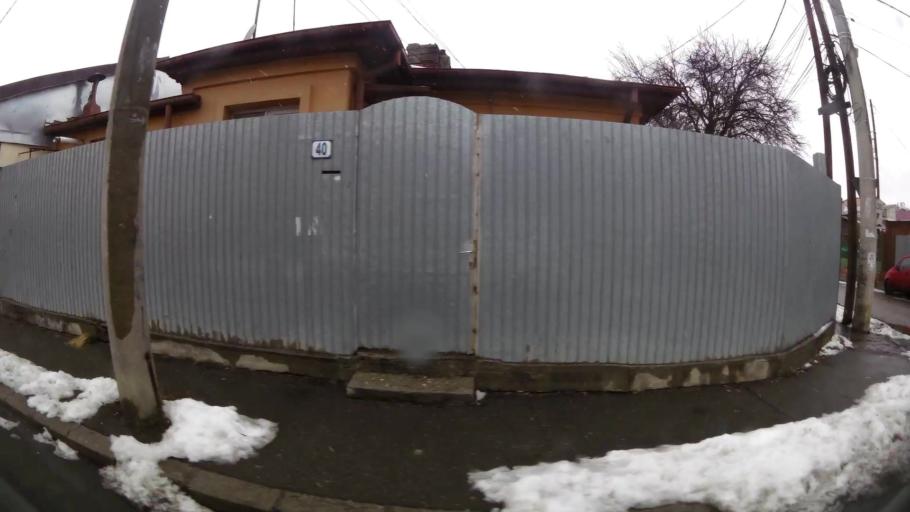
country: RO
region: Ilfov
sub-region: Comuna Mogosoaia
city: Mogosoaia
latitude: 44.4940
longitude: 26.0286
